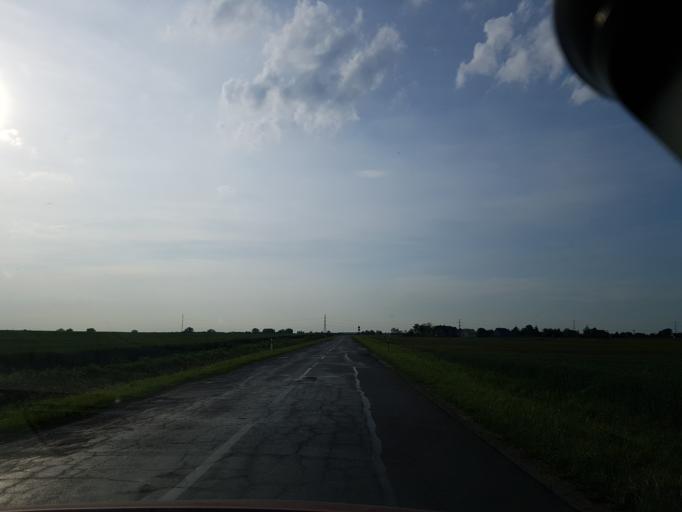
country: PL
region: Lower Silesian Voivodeship
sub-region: Powiat wroclawski
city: Gniechowice
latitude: 50.9695
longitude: 16.8686
